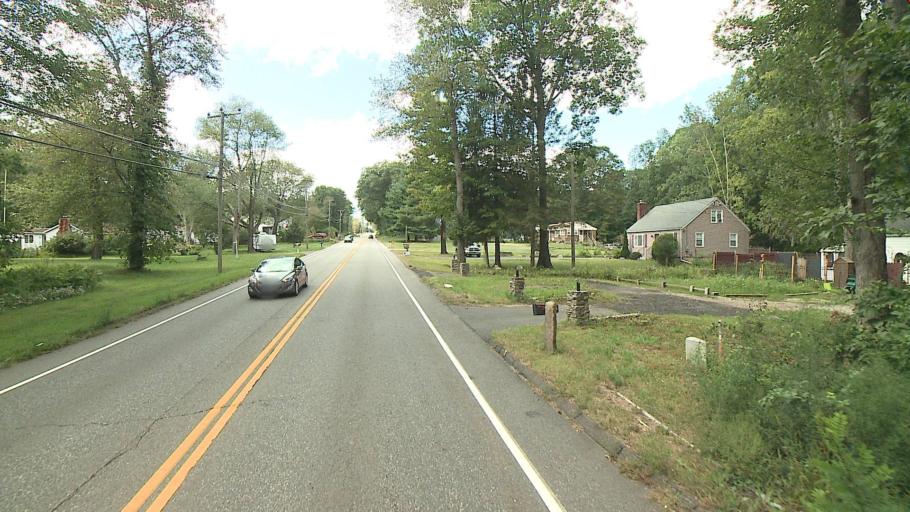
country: US
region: Connecticut
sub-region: Tolland County
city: Coventry Lake
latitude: 41.7970
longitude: -72.4002
